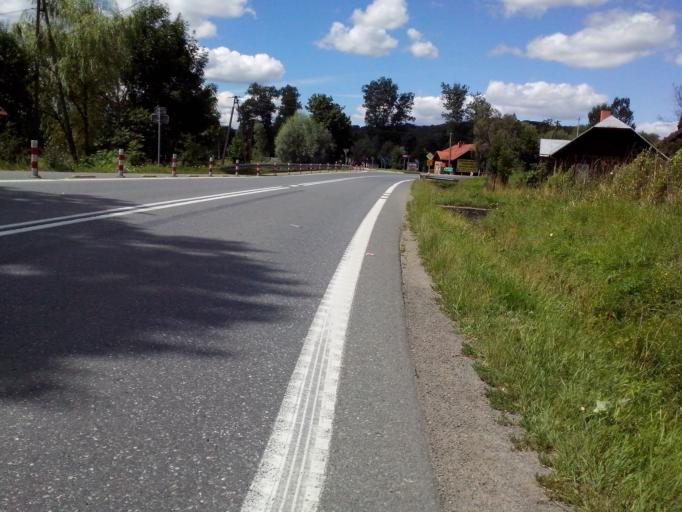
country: PL
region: Subcarpathian Voivodeship
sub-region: Powiat strzyzowski
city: Jawornik
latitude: 49.8068
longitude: 21.8869
